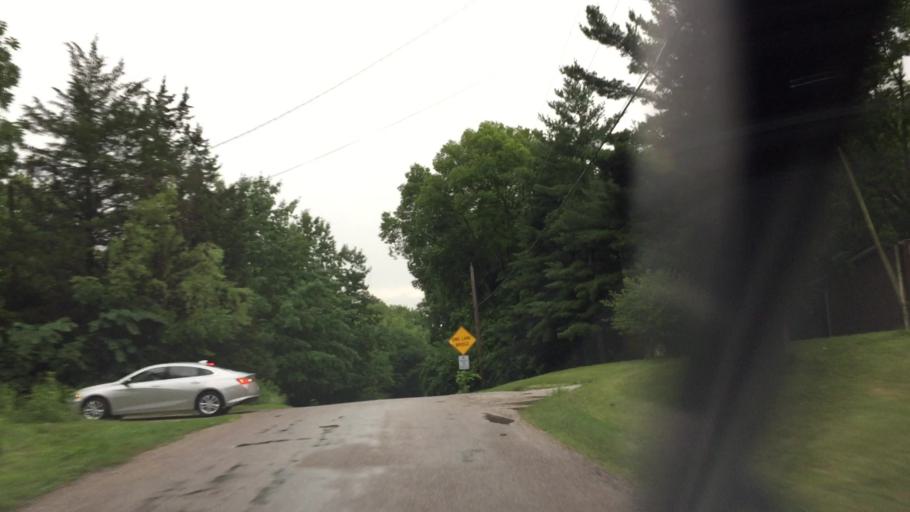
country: US
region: Illinois
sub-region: Hancock County
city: Nauvoo
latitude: 40.5378
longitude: -91.3760
